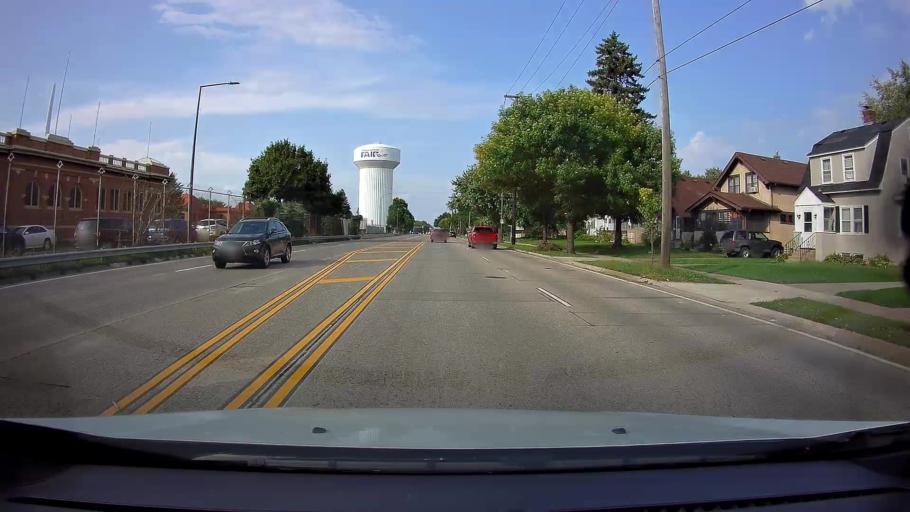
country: US
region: Minnesota
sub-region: Ramsey County
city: Falcon Heights
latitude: 44.9838
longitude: -93.1670
